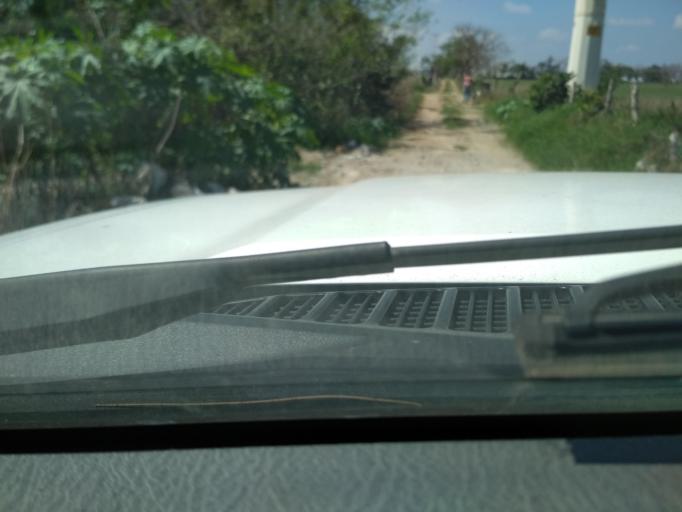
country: MX
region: Veracruz
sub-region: Veracruz
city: Las Amapolas
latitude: 19.1363
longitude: -96.2168
